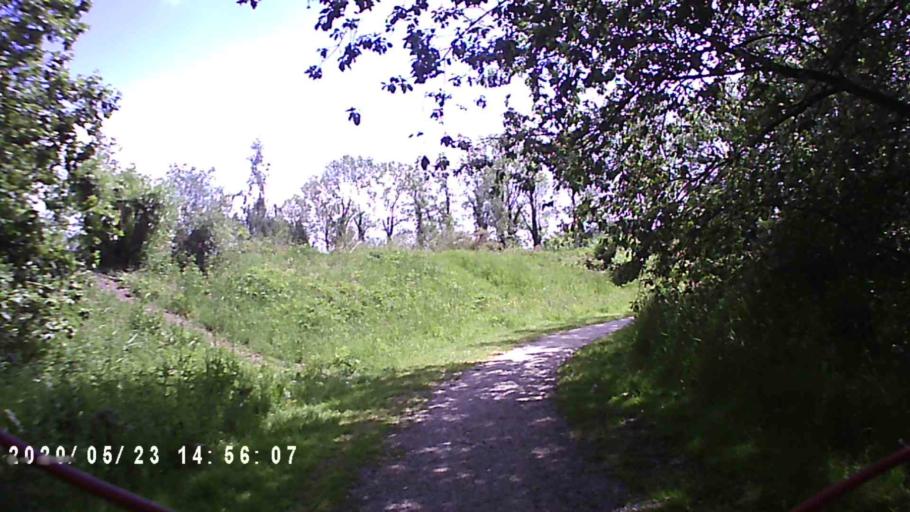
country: NL
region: Groningen
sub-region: Gemeente Delfzijl
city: Delfzijl
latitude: 53.2564
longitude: 6.9240
